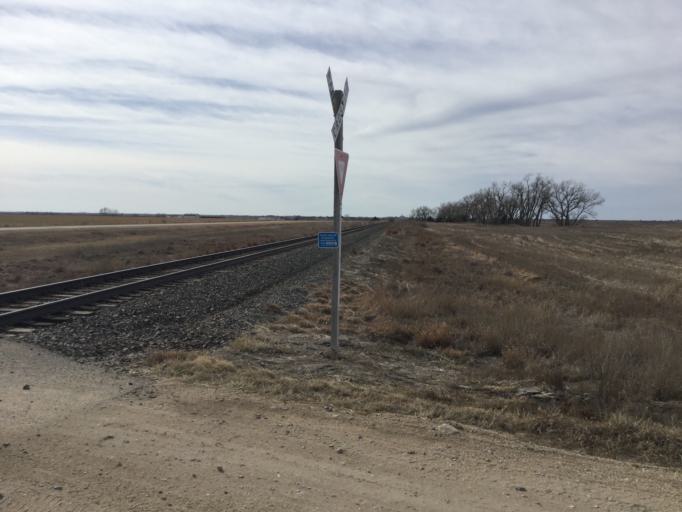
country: US
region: Kansas
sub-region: Ellis County
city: Victoria
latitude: 38.8630
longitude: -99.0954
